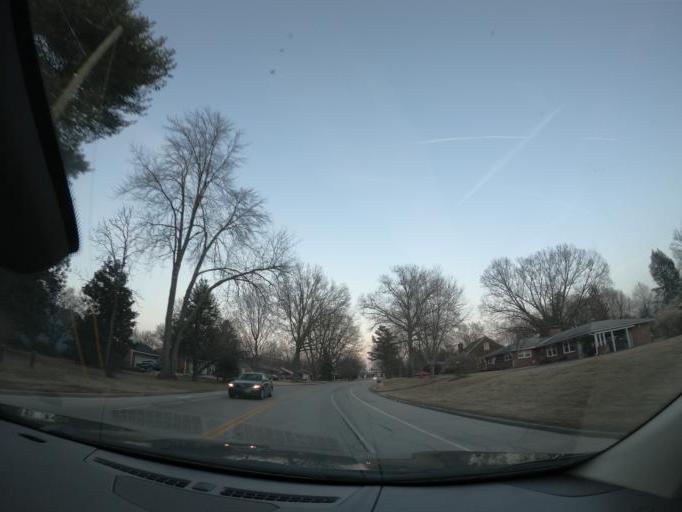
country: US
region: Kentucky
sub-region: Jefferson County
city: Lyndon
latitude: 38.2550
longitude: -85.5912
